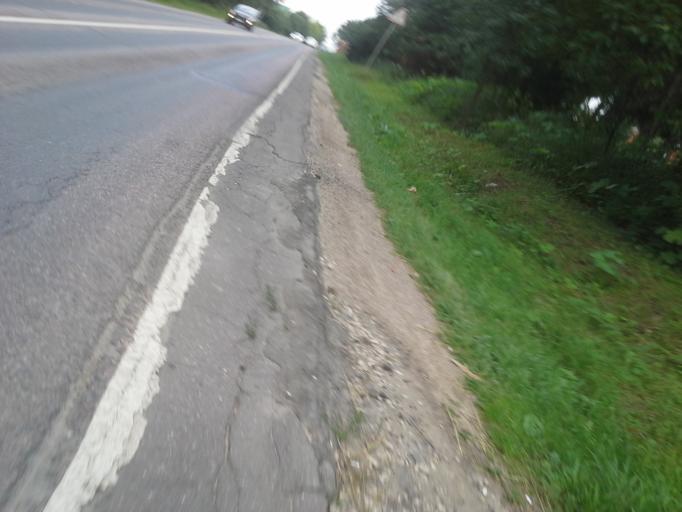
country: RU
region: Moskovskaya
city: Istra
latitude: 55.9317
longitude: 36.9281
